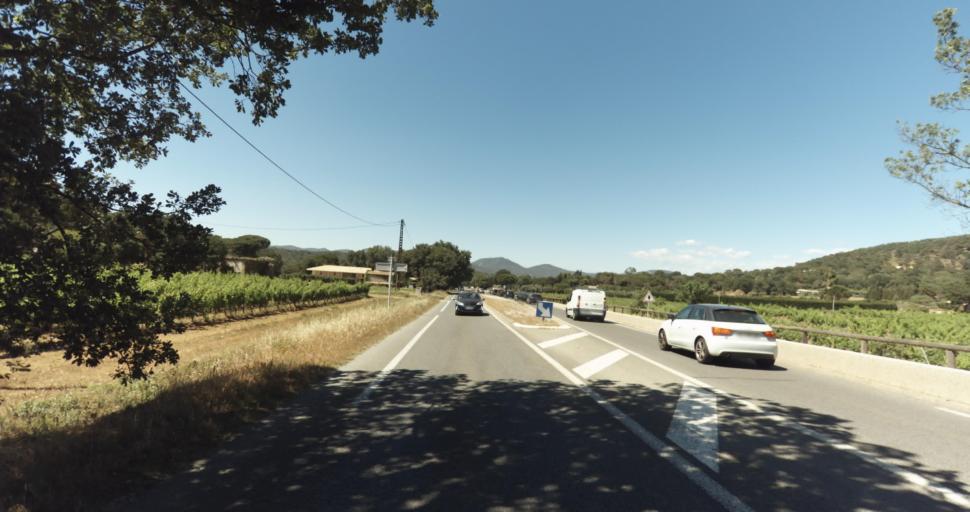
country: FR
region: Provence-Alpes-Cote d'Azur
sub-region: Departement du Var
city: Gassin
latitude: 43.2343
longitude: 6.5742
